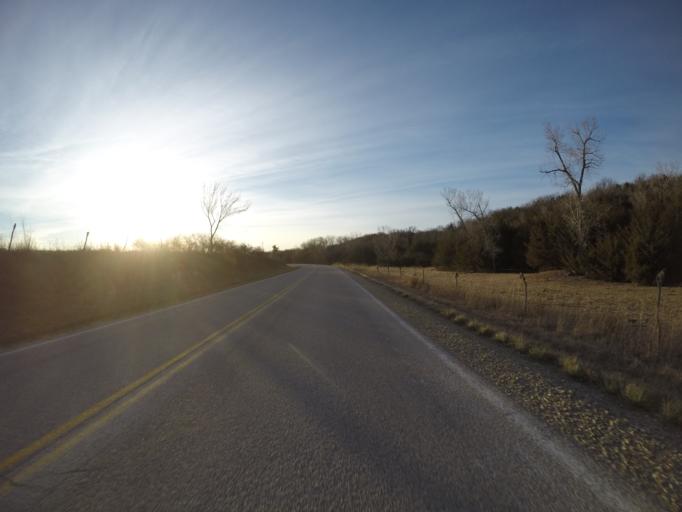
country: US
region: Kansas
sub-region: Riley County
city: Manhattan
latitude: 39.3041
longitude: -96.7139
